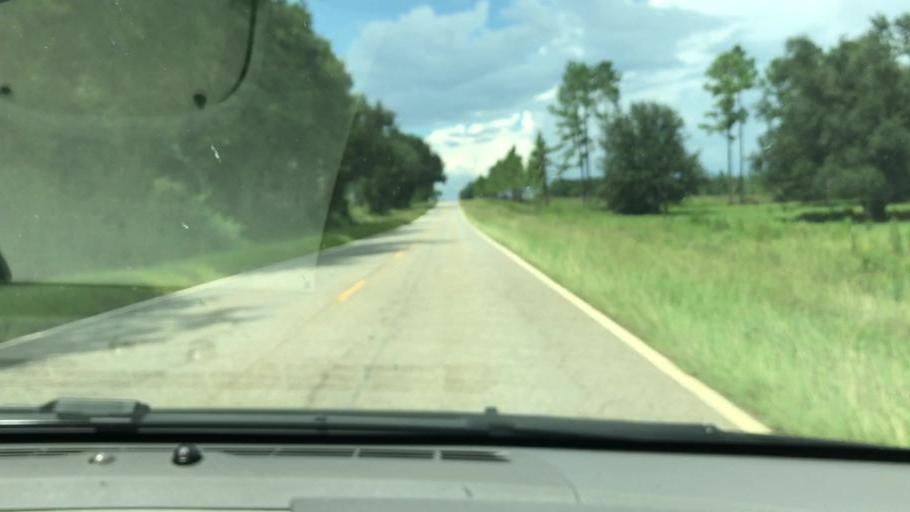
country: US
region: Georgia
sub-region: Early County
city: Blakely
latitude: 31.2684
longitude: -84.9907
